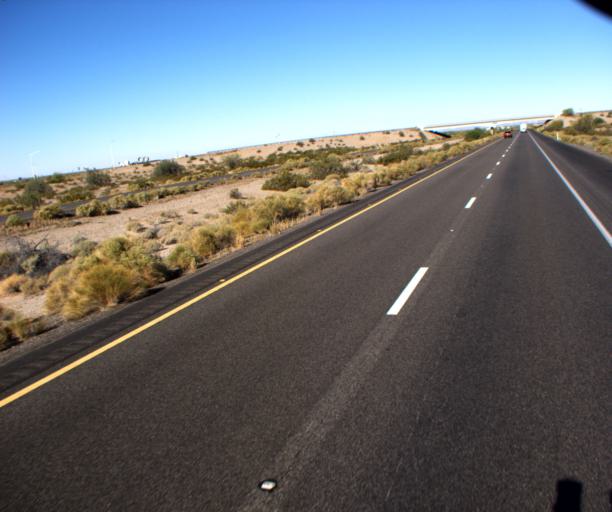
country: US
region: Arizona
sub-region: Maricopa County
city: Gila Bend
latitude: 32.9246
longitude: -112.6673
